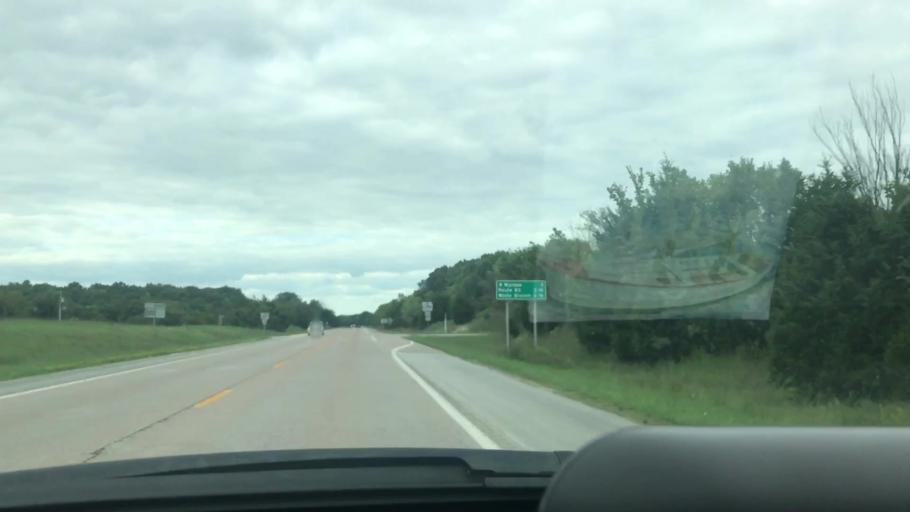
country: US
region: Missouri
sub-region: Benton County
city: Warsaw
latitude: 38.1947
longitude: -93.3247
